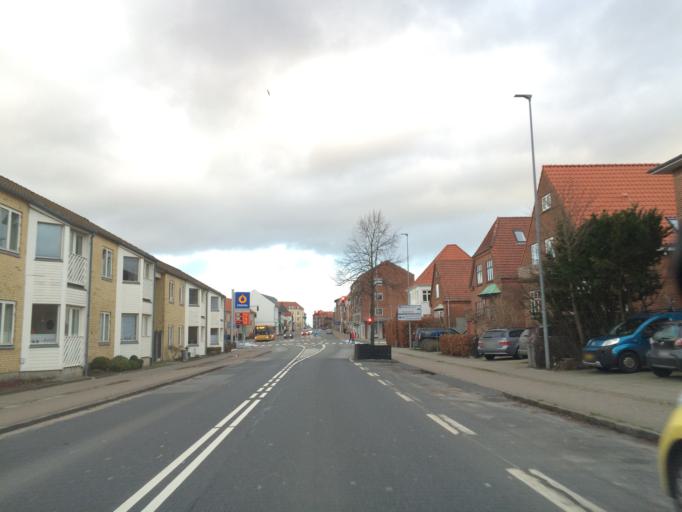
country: DK
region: Central Jutland
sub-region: Silkeborg Kommune
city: Silkeborg
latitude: 56.1620
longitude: 9.5507
